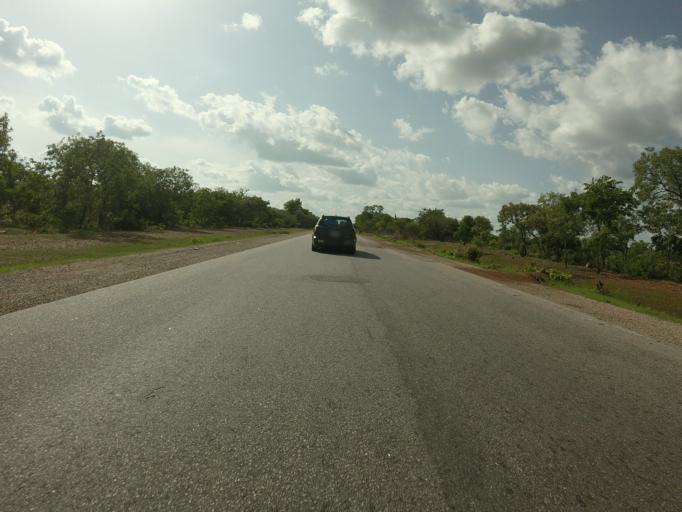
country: GH
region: Upper East
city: Bolgatanga
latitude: 10.5273
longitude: -0.8163
